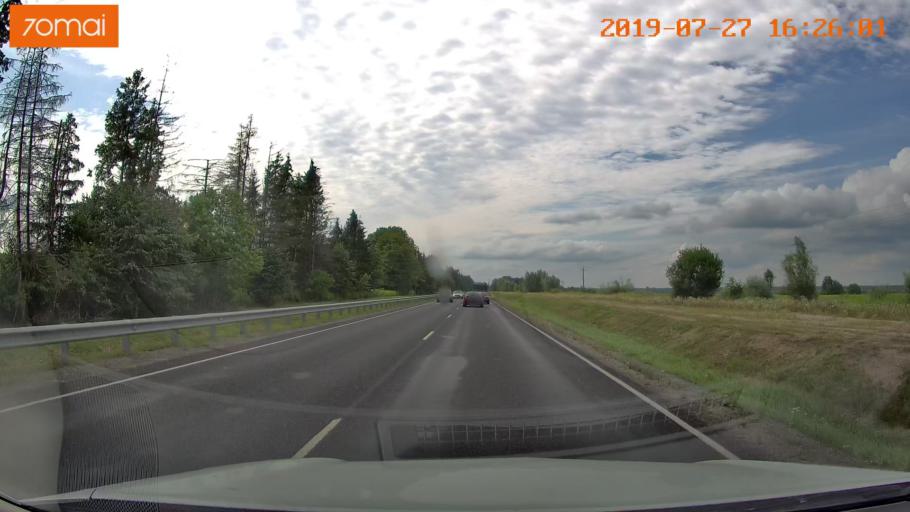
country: RU
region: Kaliningrad
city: Zheleznodorozhnyy
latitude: 54.6391
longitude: 21.4193
